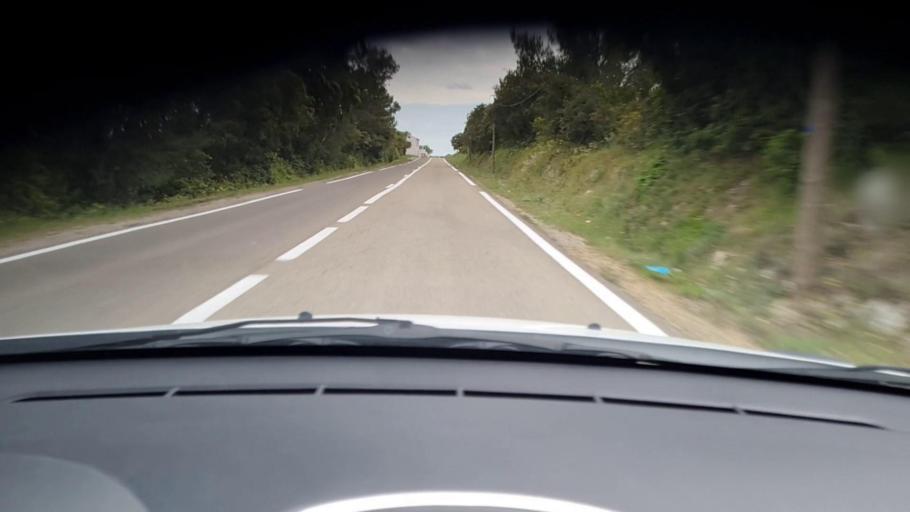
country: FR
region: Languedoc-Roussillon
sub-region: Departement du Gard
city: Poulx
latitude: 43.8792
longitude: 4.3796
